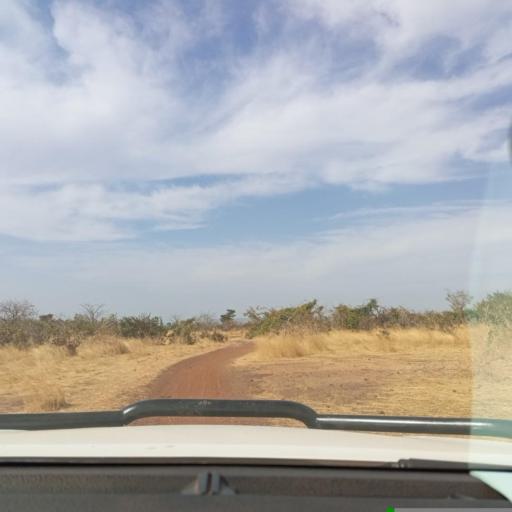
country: ML
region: Koulikoro
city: Kati
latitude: 12.7470
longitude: -8.2504
